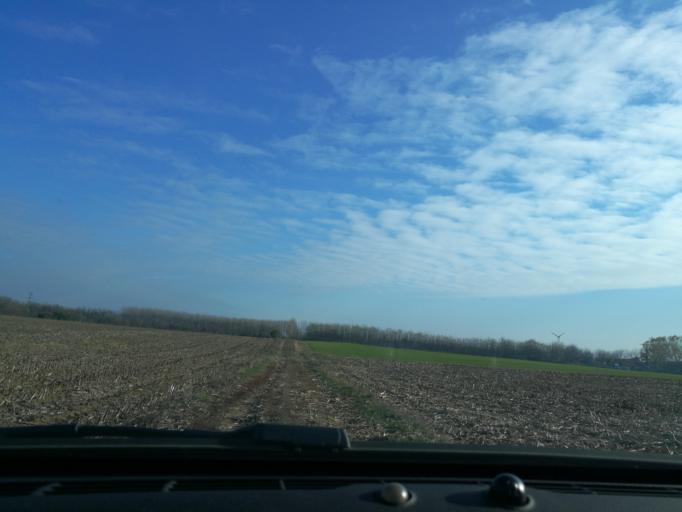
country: HU
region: Szabolcs-Szatmar-Bereg
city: Nyiregyhaza
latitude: 47.9579
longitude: 21.7596
